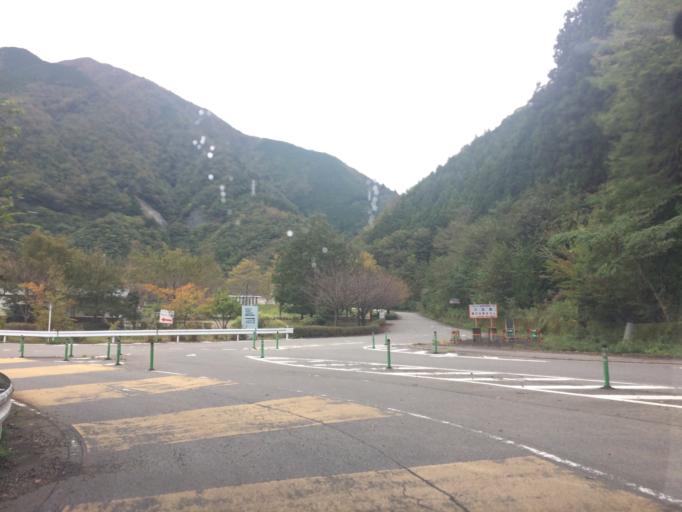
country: JP
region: Shizuoka
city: Shizuoka-shi
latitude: 35.1644
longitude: 138.1512
